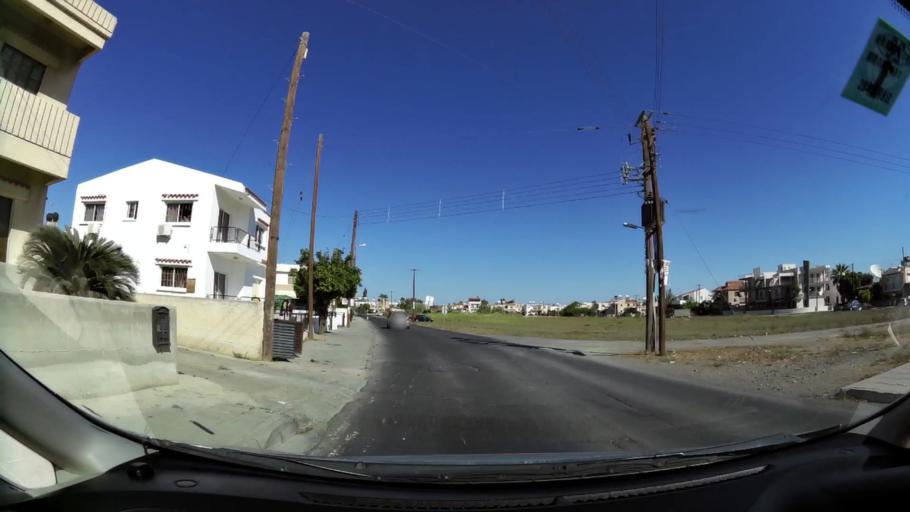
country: CY
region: Larnaka
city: Livadia
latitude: 34.9405
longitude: 33.6283
